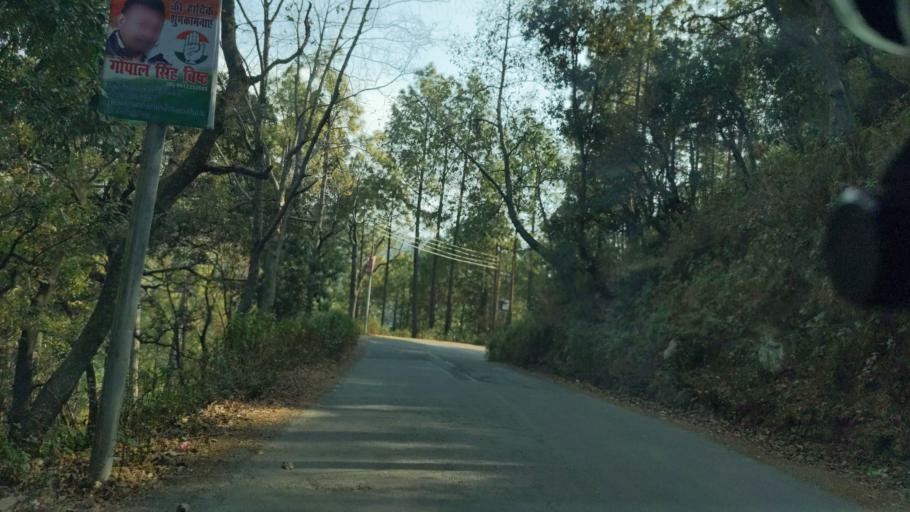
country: IN
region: Uttarakhand
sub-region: Naini Tal
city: Bhowali
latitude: 29.4045
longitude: 79.5392
